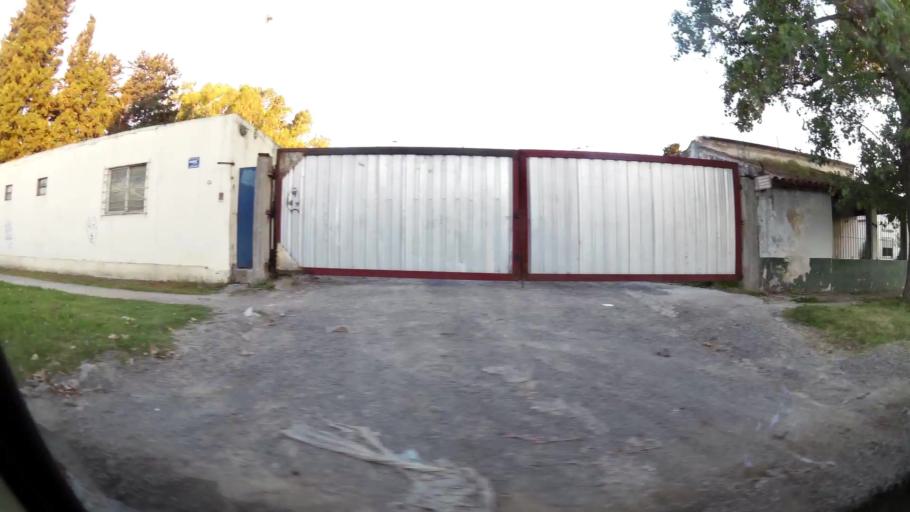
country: AR
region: Buenos Aires
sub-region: Partido de Quilmes
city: Quilmes
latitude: -34.8157
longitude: -58.1923
